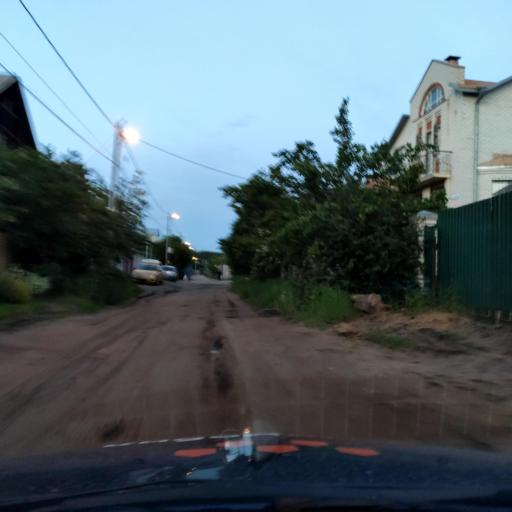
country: RU
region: Voronezj
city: Podgornoye
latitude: 51.7469
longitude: 39.1531
